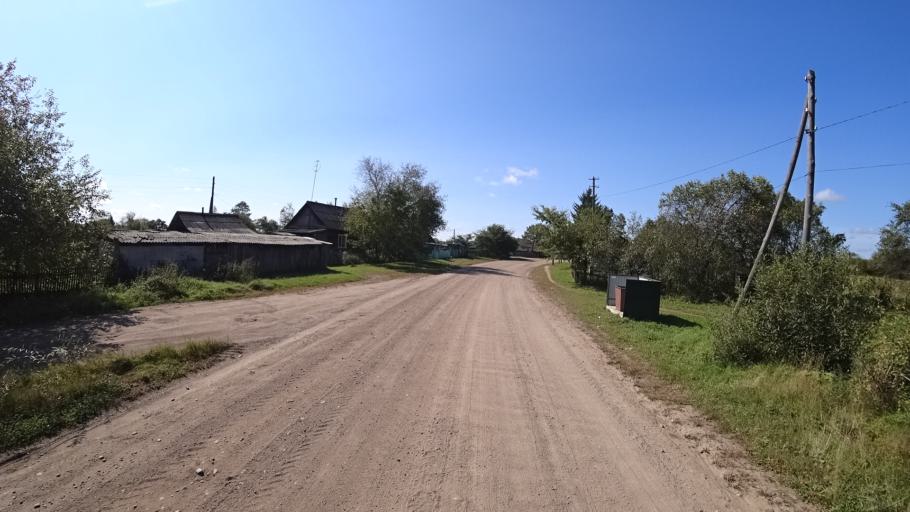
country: RU
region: Amur
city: Arkhara
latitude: 49.4021
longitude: 130.1507
